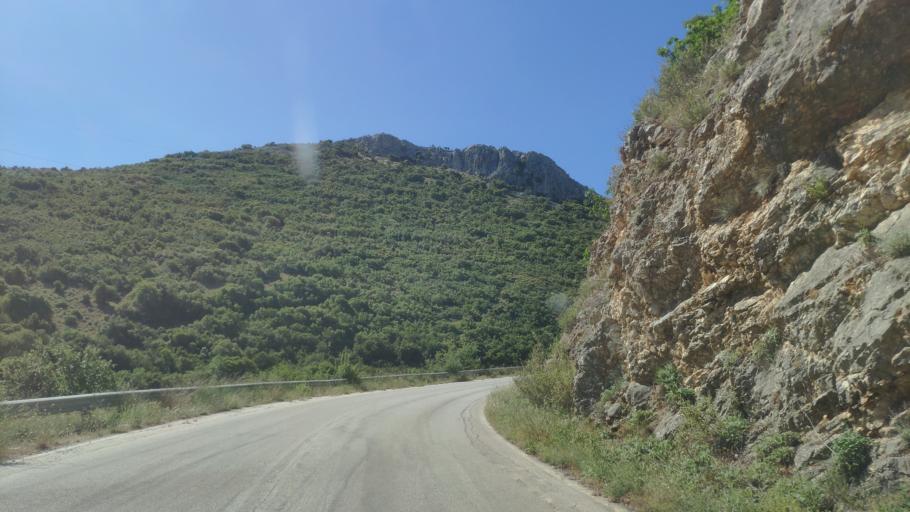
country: GR
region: Peloponnese
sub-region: Nomos Korinthias
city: Khiliomodhi
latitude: 37.7691
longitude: 22.8839
